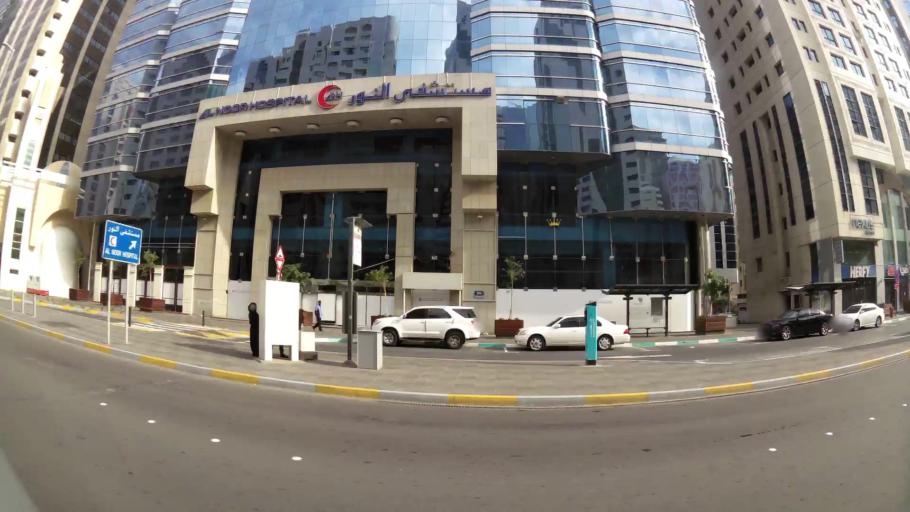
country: AE
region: Abu Dhabi
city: Abu Dhabi
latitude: 24.4908
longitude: 54.3608
